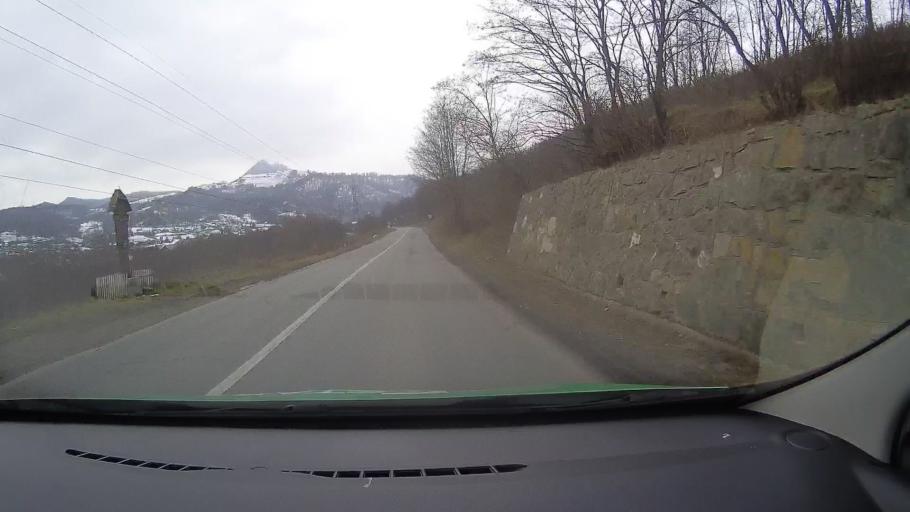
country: RO
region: Alba
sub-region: Oras Zlatna
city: Fenes
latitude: 46.0909
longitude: 23.2730
